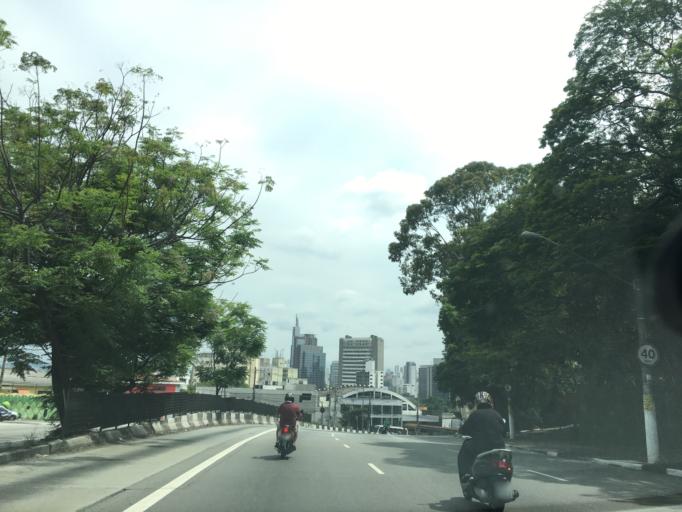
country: BR
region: Sao Paulo
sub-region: Sao Paulo
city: Sao Paulo
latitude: -23.5742
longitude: -46.7065
